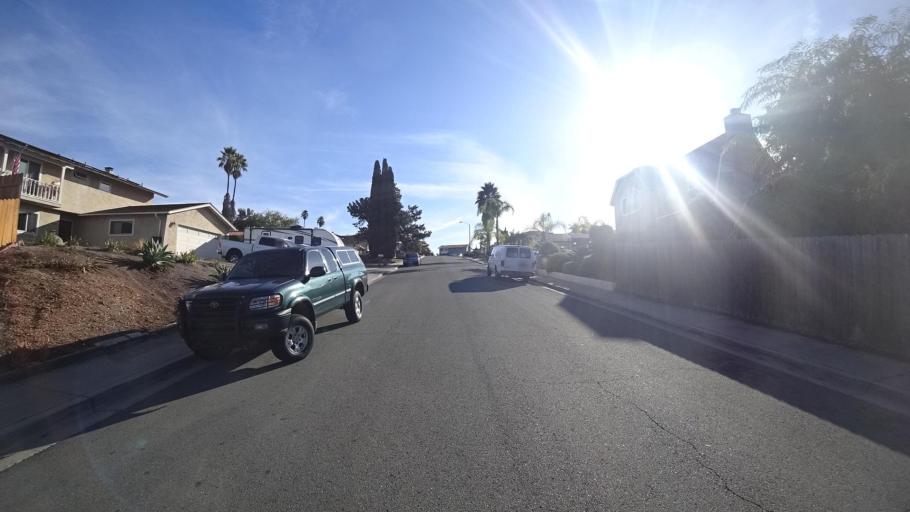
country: US
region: California
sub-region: San Diego County
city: Spring Valley
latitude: 32.7383
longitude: -116.9786
